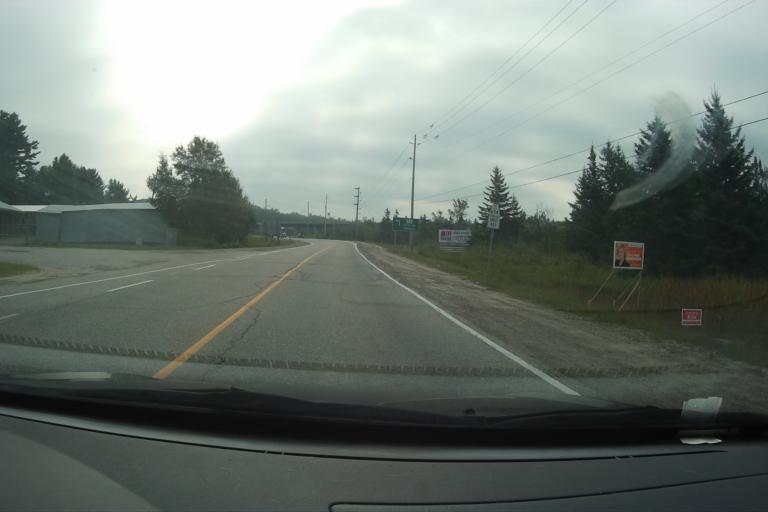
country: CA
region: Ontario
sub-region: Nipissing District
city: North Bay
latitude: 46.1975
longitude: -79.3599
